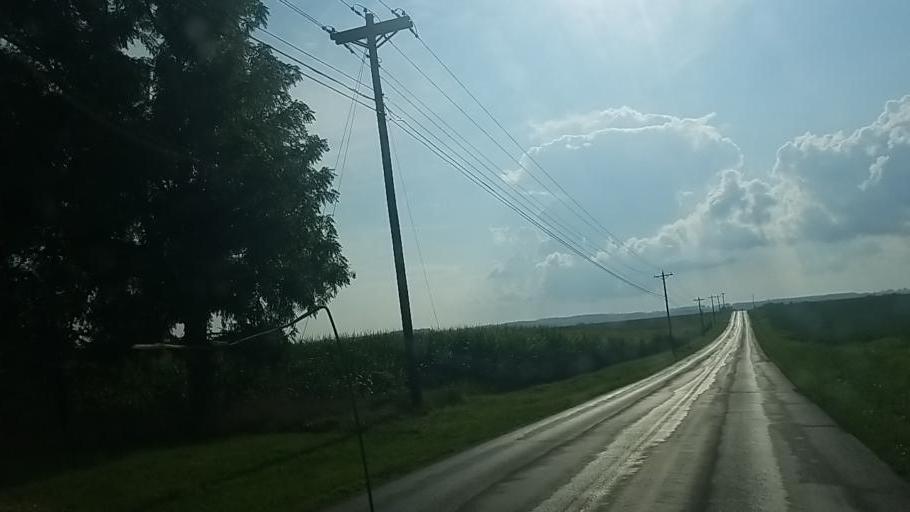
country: US
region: Ohio
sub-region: Wayne County
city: Wooster
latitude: 40.8582
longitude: -81.9840
